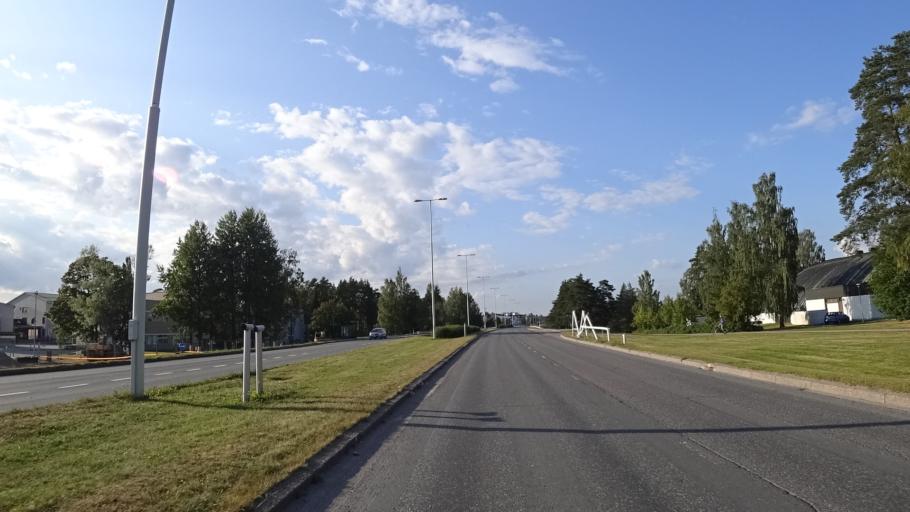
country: FI
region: South Karelia
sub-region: Imatra
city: Imatra
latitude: 61.1851
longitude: 28.7788
